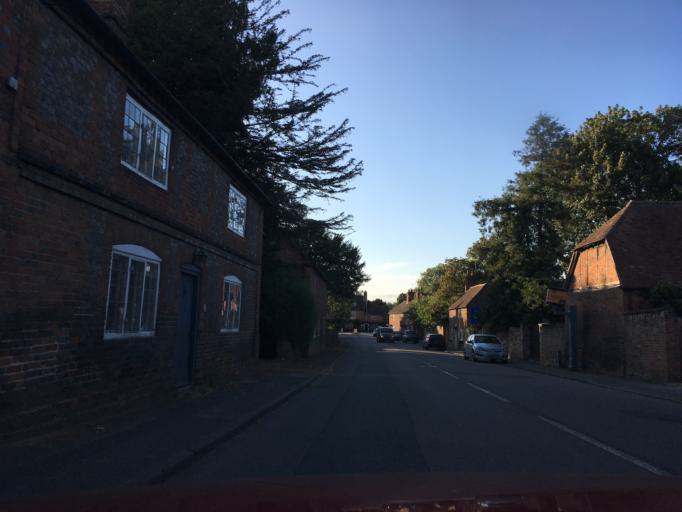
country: GB
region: England
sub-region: Hampshire
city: Tadley
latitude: 51.3827
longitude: -1.1524
